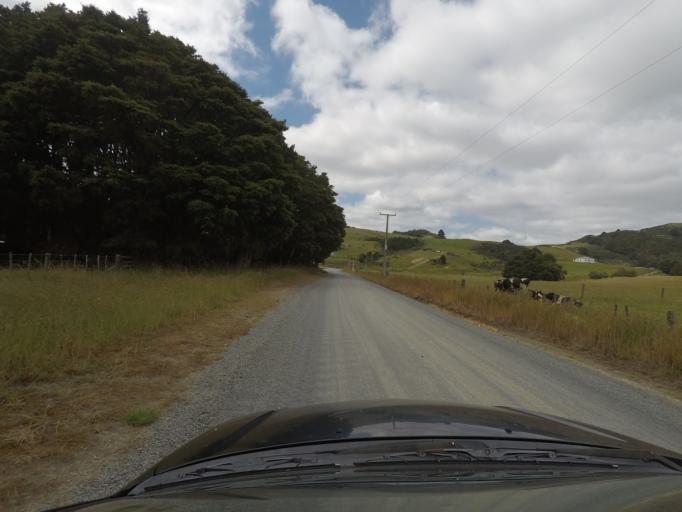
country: NZ
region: Northland
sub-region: Whangarei
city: Ruakaka
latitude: -35.9337
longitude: 174.3475
